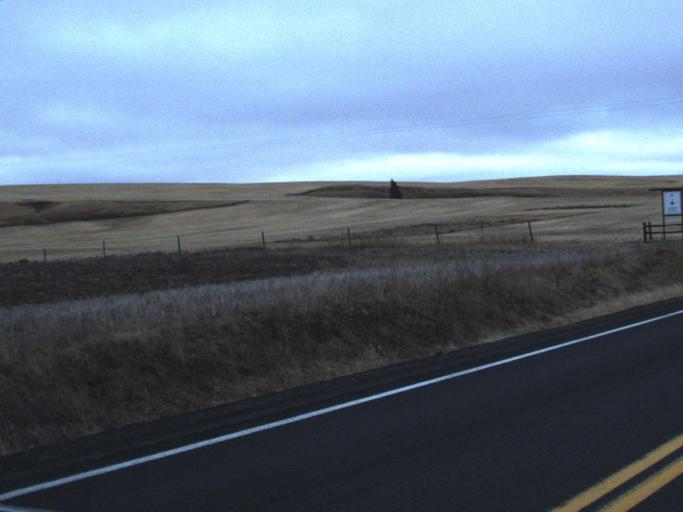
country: US
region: Washington
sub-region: Spokane County
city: Medical Lake
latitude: 47.7019
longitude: -117.8777
